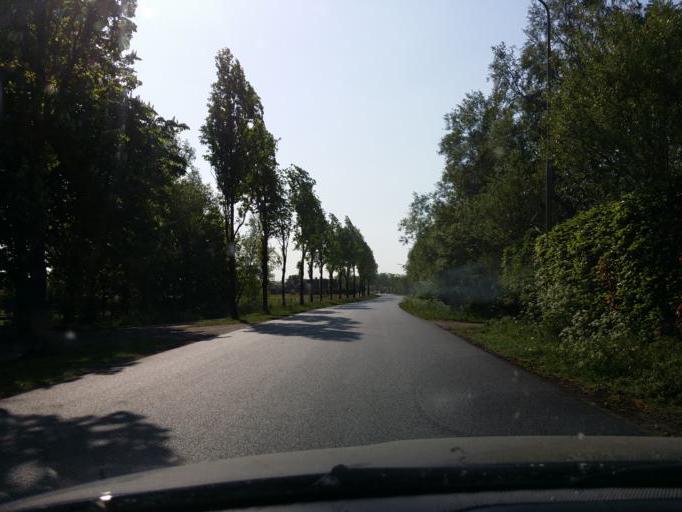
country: NL
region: Groningen
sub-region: Gemeente Zuidhorn
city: Grijpskerk
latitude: 53.2212
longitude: 6.3255
